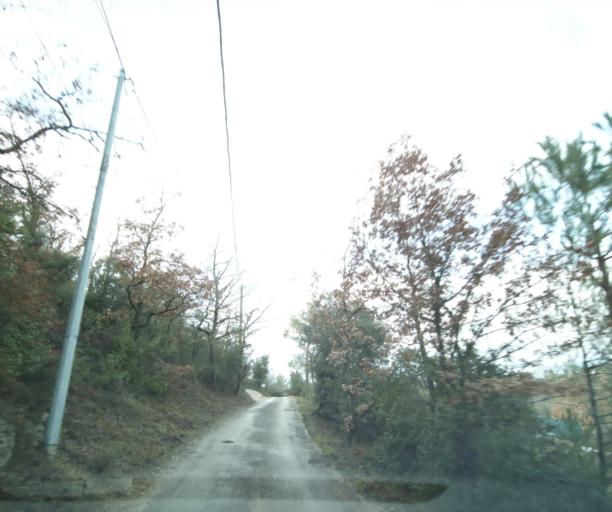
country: FR
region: Provence-Alpes-Cote d'Azur
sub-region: Departement du Var
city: Tourves
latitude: 43.4026
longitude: 5.9071
